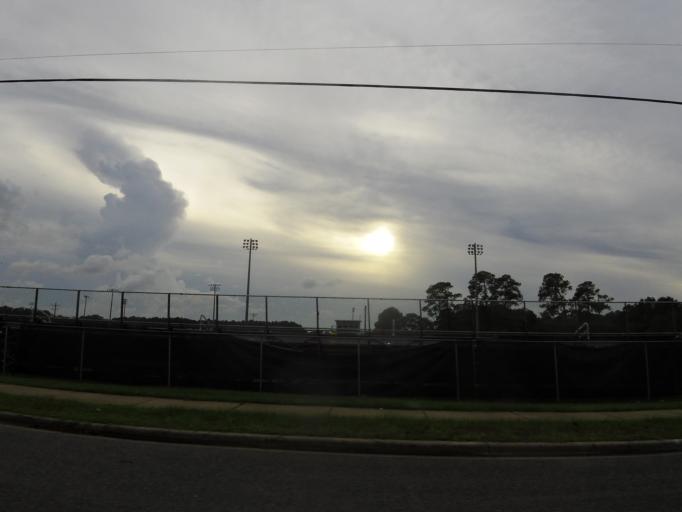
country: US
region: Florida
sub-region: Duval County
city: Jacksonville
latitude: 30.3474
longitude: -81.7229
